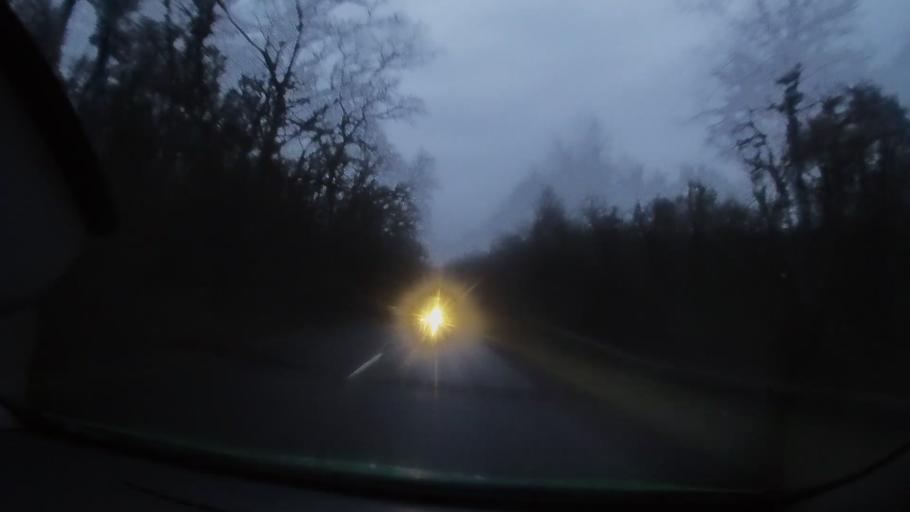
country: RO
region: Mures
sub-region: Municipiul Reghin
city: Iernuteni
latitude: 46.7694
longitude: 24.7357
